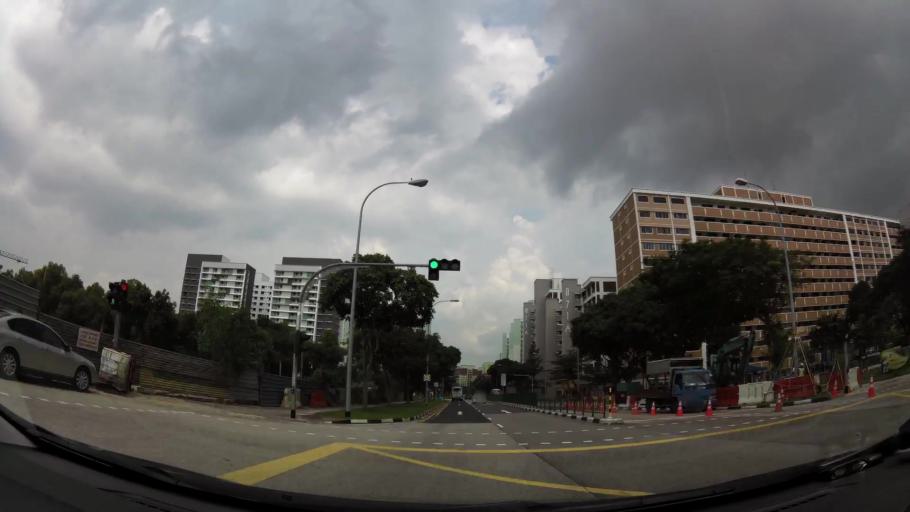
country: SG
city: Singapore
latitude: 1.3536
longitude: 103.9310
